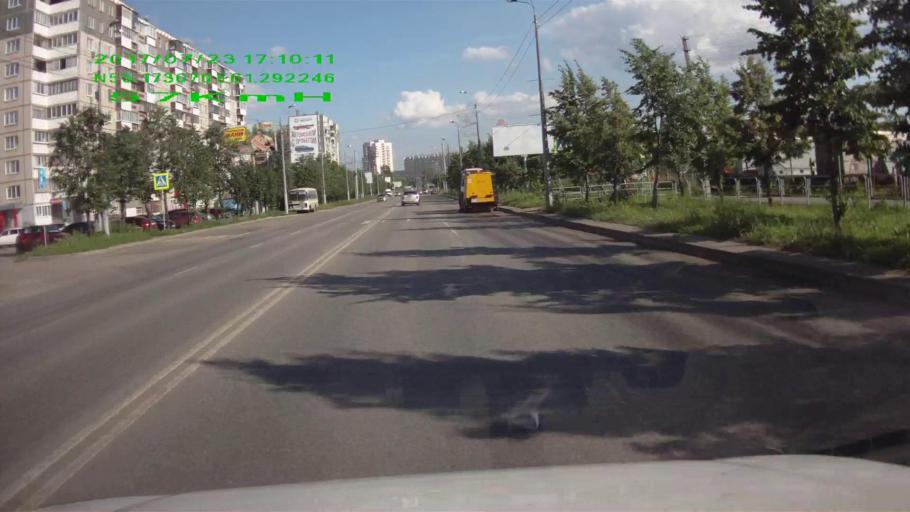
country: RU
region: Chelyabinsk
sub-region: Gorod Chelyabinsk
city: Chelyabinsk
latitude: 55.1727
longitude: 61.2927
